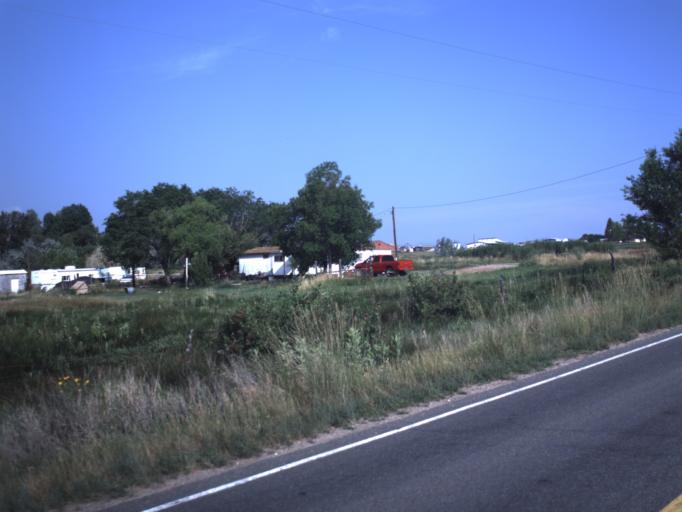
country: US
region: Utah
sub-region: Duchesne County
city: Duchesne
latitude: 40.3045
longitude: -110.2408
